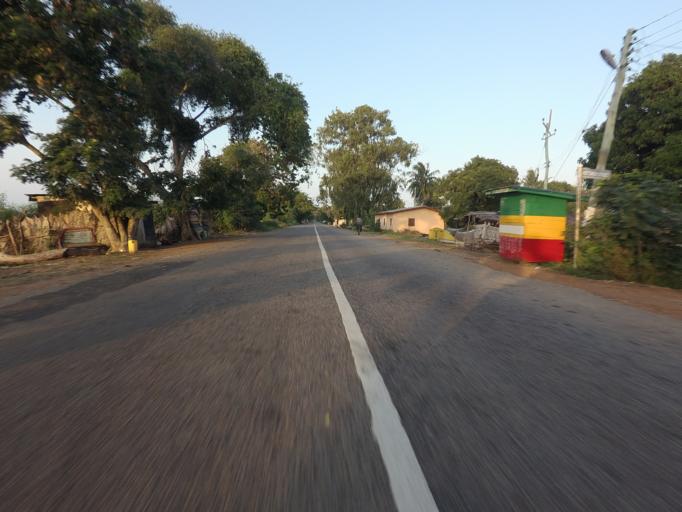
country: GH
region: Volta
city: Anloga
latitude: 5.7905
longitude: 0.8705
